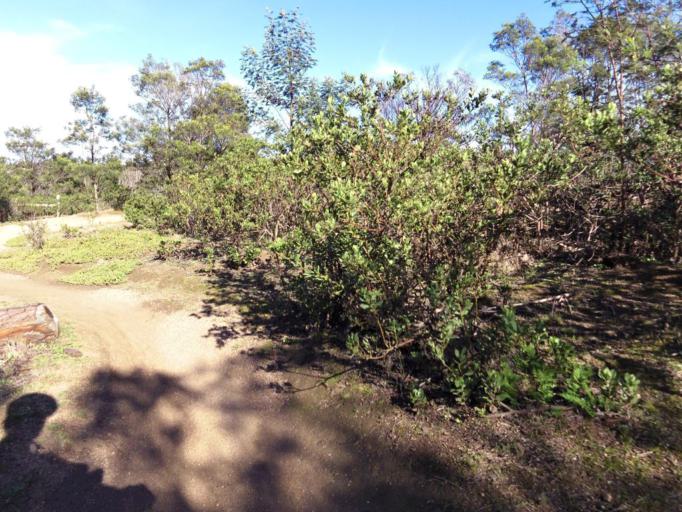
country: AU
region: Victoria
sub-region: Wyndham
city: Little River
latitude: -37.9283
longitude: 144.4307
